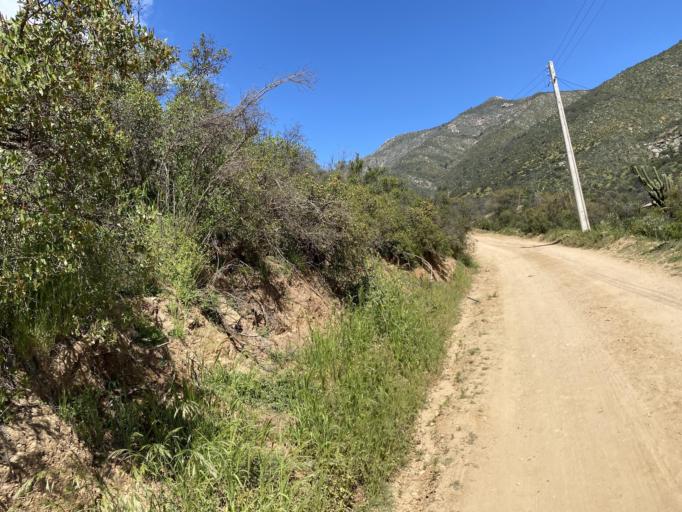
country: CL
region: Santiago Metropolitan
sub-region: Provincia de Chacabuco
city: Lampa
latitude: -33.1976
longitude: -71.0908
